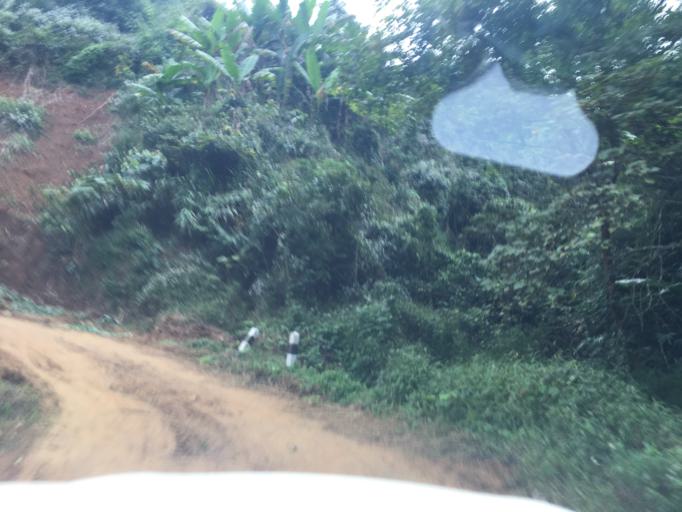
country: LA
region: Houaphan
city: Viengthong
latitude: 19.9381
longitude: 103.2916
